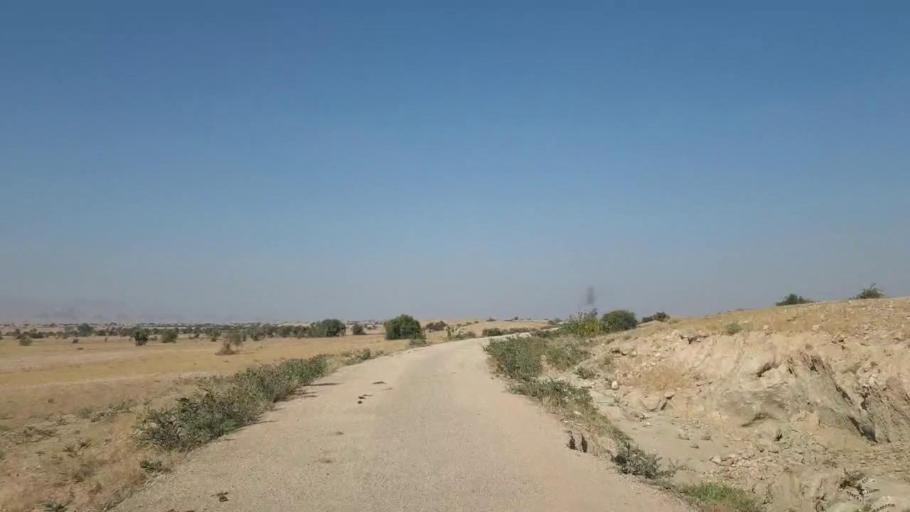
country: PK
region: Sindh
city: Jamshoro
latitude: 25.4898
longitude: 67.8392
